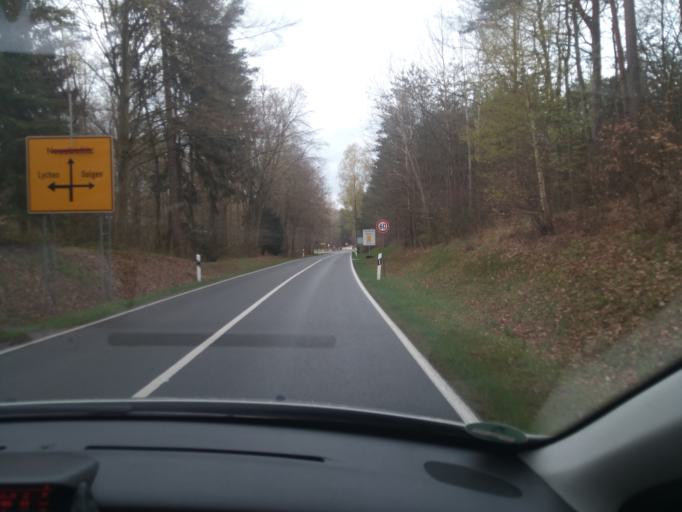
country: DE
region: Mecklenburg-Vorpommern
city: Carpin
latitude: 53.3228
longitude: 13.3406
